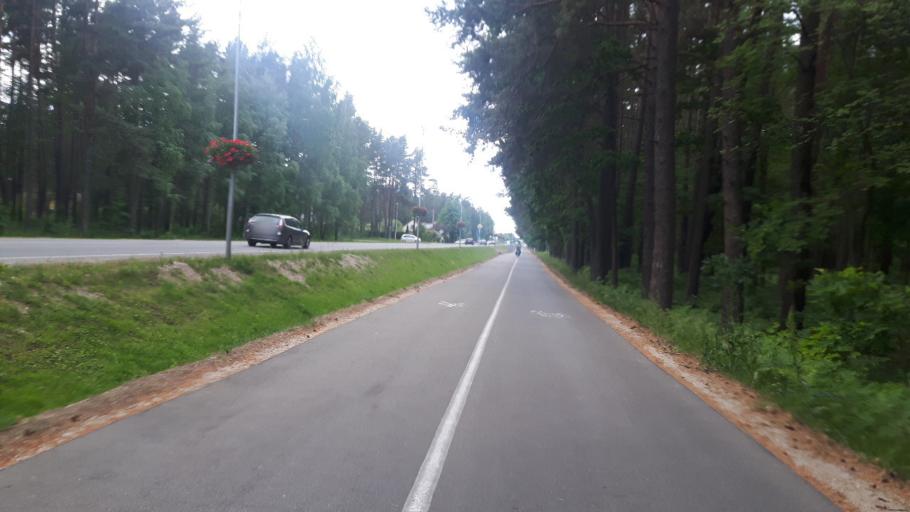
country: LV
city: Tireli
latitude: 56.9581
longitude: 23.6316
